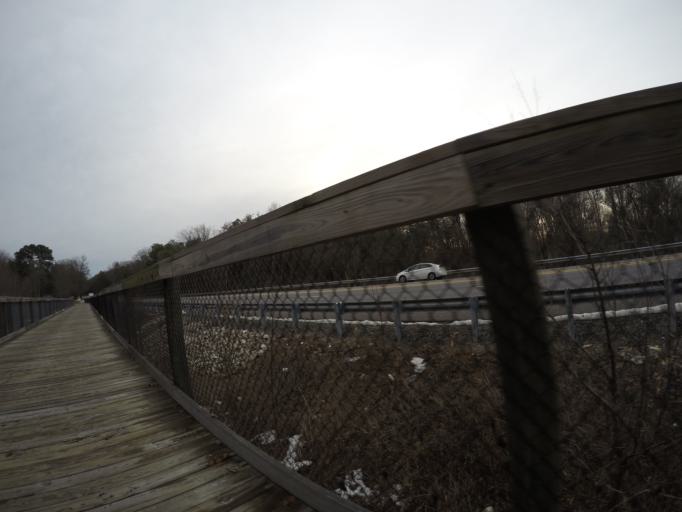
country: US
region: Maryland
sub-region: Anne Arundel County
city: Severn
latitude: 39.1680
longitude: -76.6950
